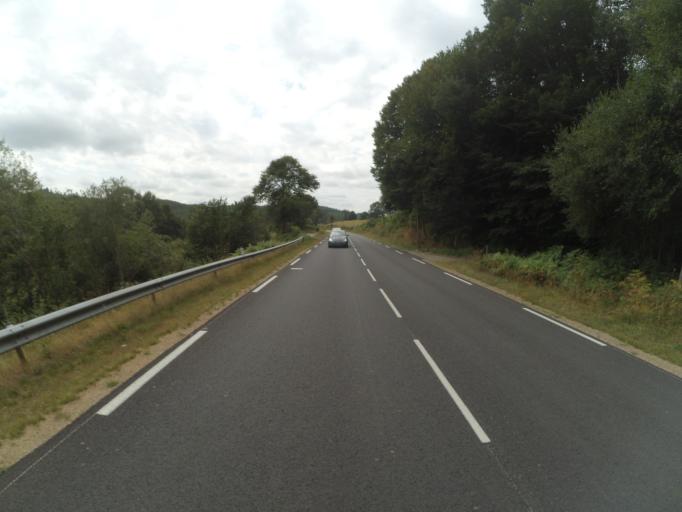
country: FR
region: Limousin
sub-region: Departement de la Creuse
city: La Courtine
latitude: 45.6380
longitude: 2.2759
